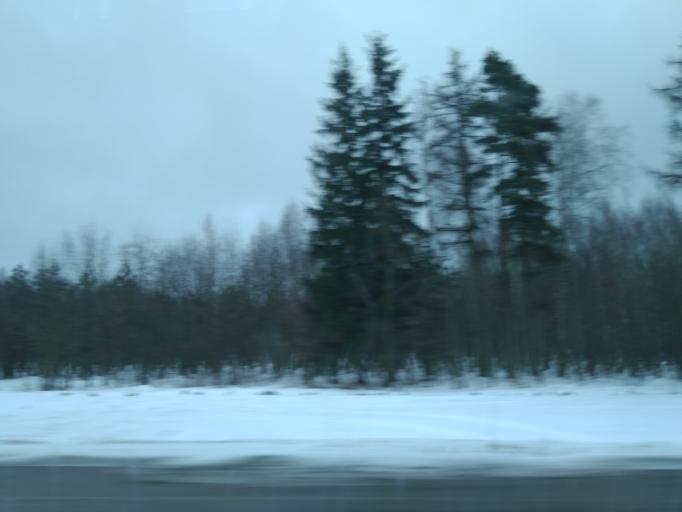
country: BY
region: Minsk
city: Nyasvizh
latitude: 53.2566
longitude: 26.6148
